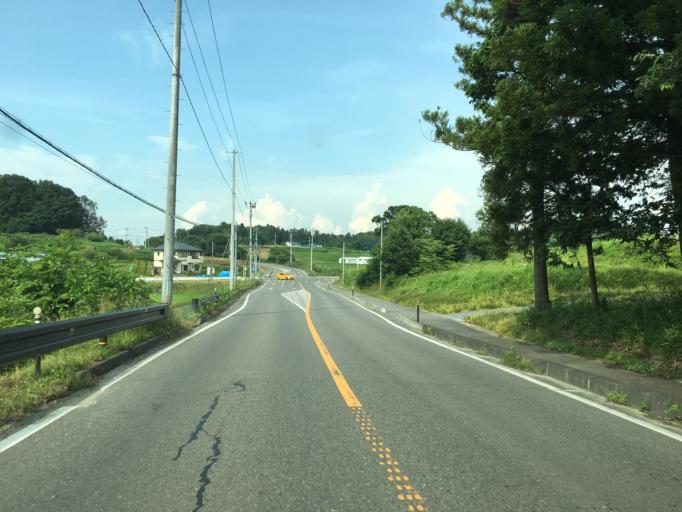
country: JP
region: Fukushima
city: Koriyama
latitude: 37.3550
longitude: 140.4152
